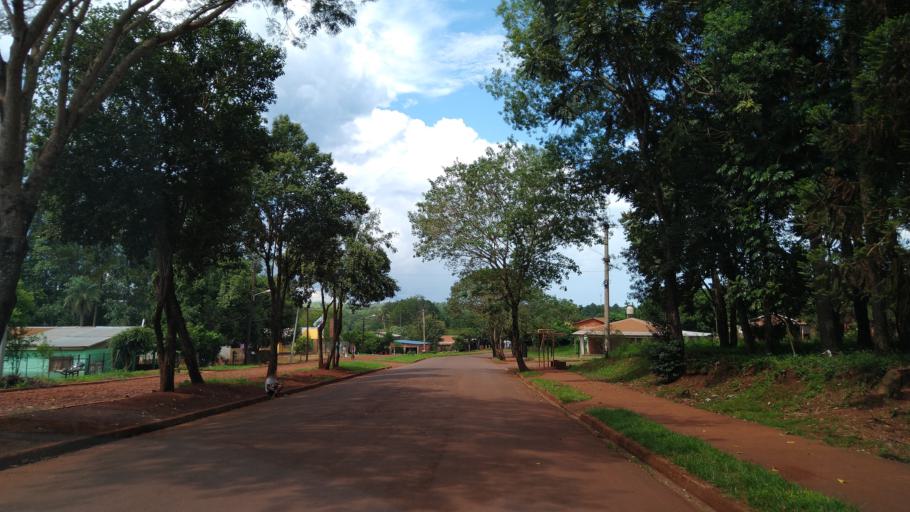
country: AR
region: Misiones
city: Puerto Libertad
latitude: -25.9669
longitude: -54.5911
